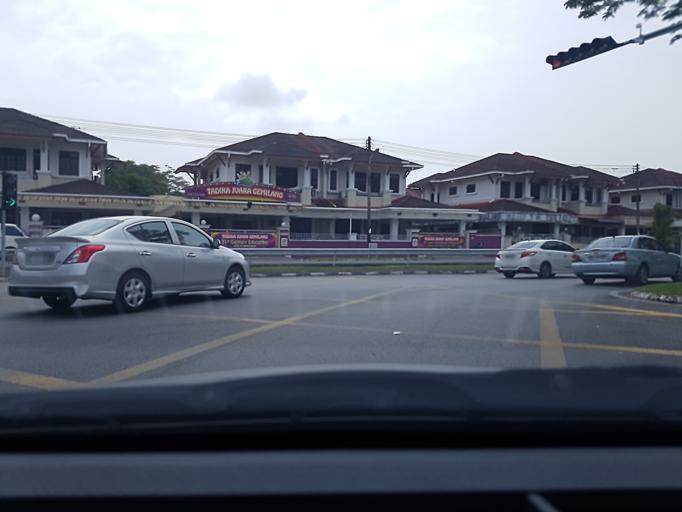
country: MY
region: Sarawak
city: Kuching
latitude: 1.5178
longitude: 110.3632
